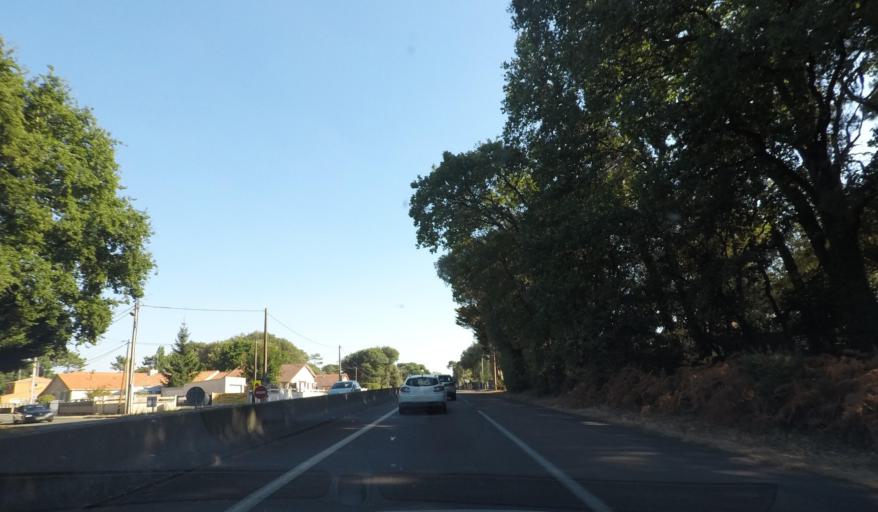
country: FR
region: Pays de la Loire
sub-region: Departement de la Loire-Atlantique
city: Saint-Michel-Chef-Chef
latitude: 47.2076
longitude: -2.1499
